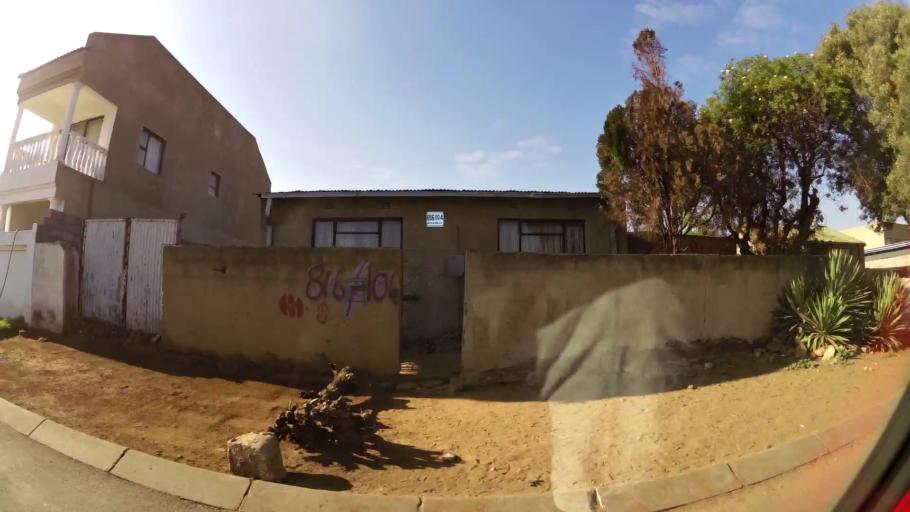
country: ZA
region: Gauteng
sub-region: City of Johannesburg Metropolitan Municipality
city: Soweto
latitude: -26.2368
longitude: 27.9251
